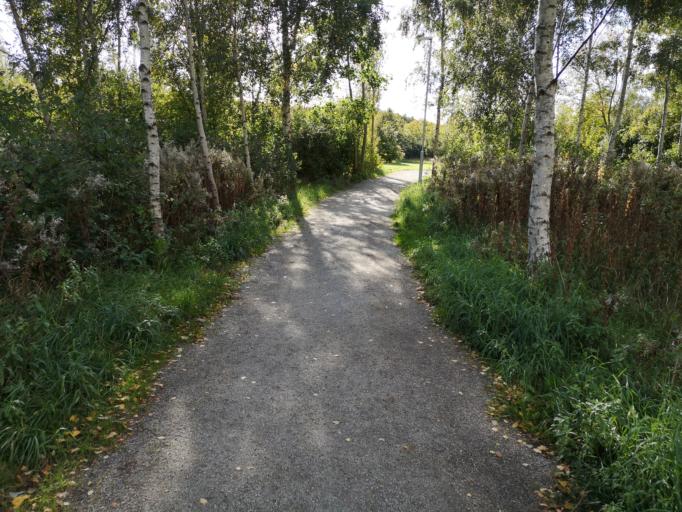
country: SE
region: Skane
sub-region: Kavlinge Kommun
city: Kaevlinge
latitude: 55.8016
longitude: 13.1034
